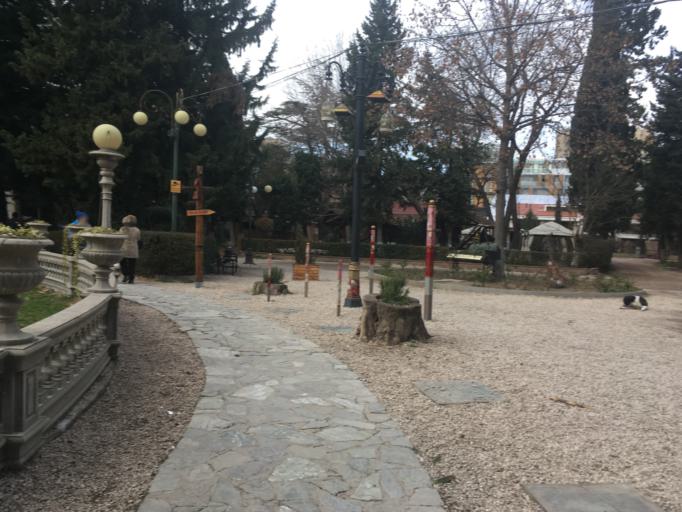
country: GE
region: T'bilisi
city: Tbilisi
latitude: 41.7083
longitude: 44.7999
